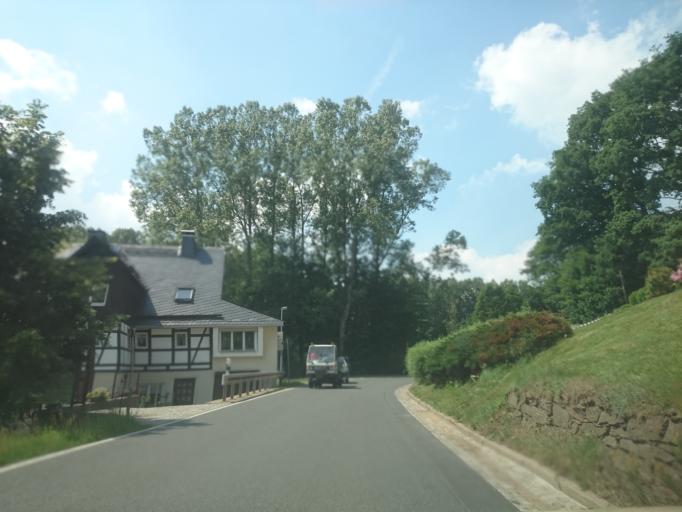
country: DE
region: Saxony
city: Oberschona
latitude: 50.8755
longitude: 13.2828
